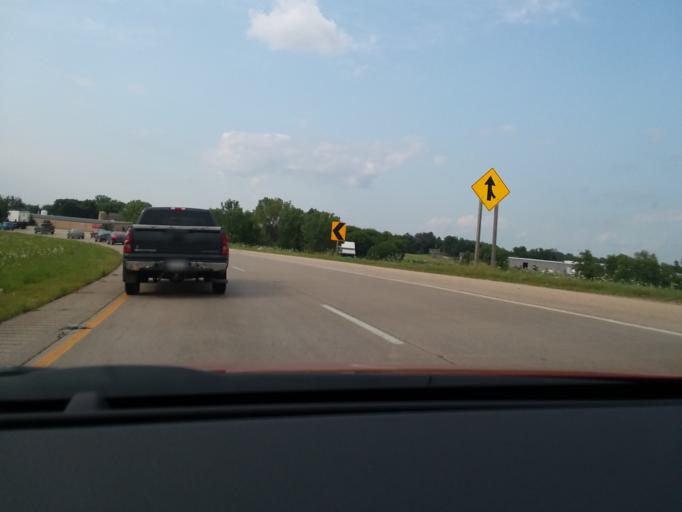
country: US
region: Wisconsin
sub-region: Dane County
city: McFarland
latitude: 43.0481
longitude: -89.2731
